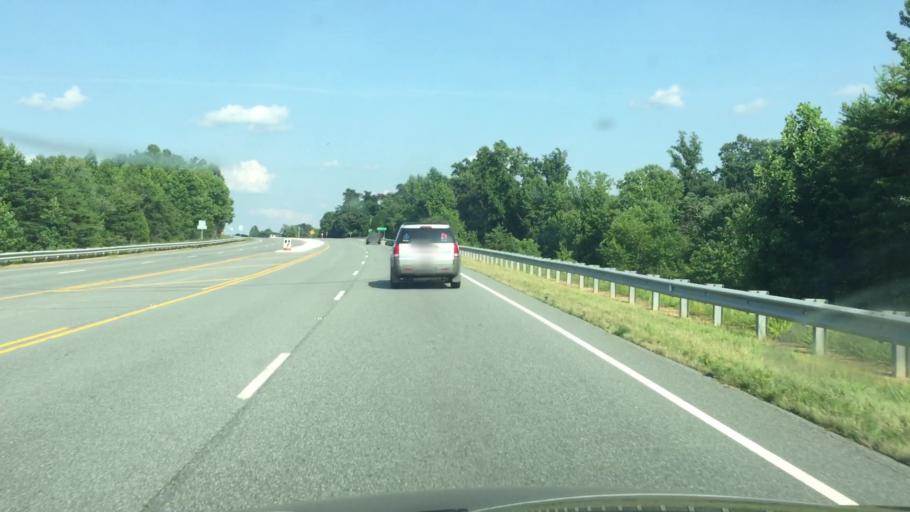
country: US
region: North Carolina
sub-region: Rockingham County
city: Reidsville
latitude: 36.3620
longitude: -79.6360
